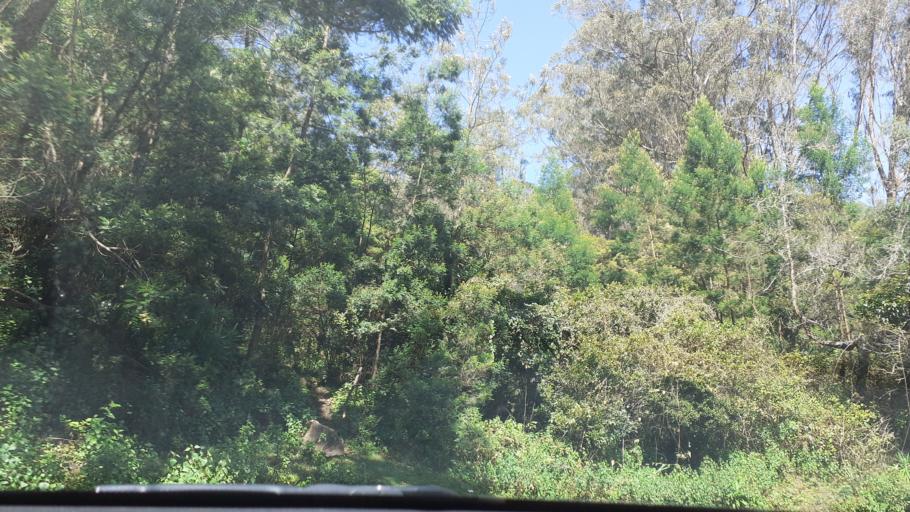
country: IN
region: Tamil Nadu
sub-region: Dindigul
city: Kodaikanal
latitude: 10.2220
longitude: 77.4205
